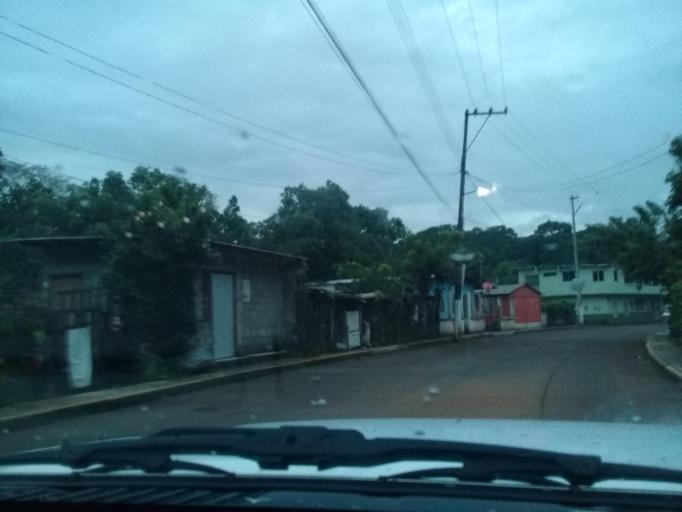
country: MX
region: Veracruz
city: San Andres Tuxtla
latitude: 18.4408
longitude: -95.2217
